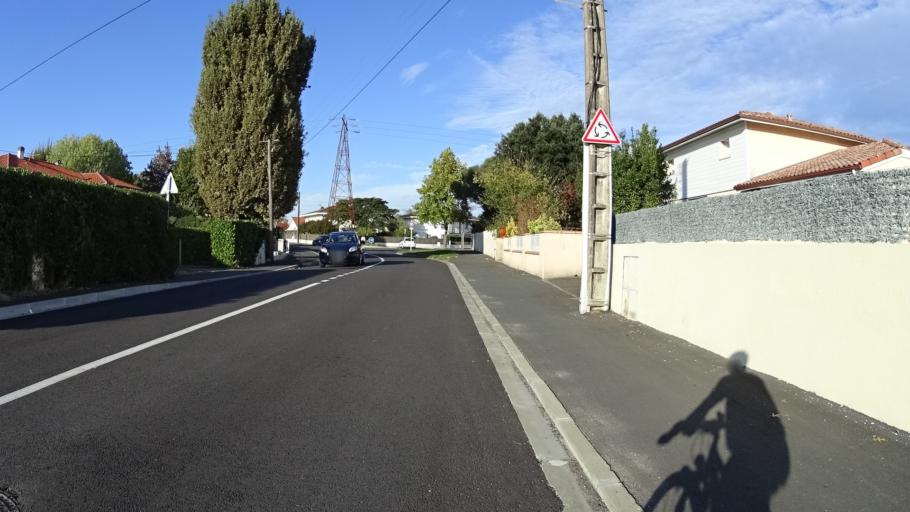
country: FR
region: Aquitaine
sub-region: Departement des Landes
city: Saint-Paul-les-Dax
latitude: 43.7347
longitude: -1.0544
